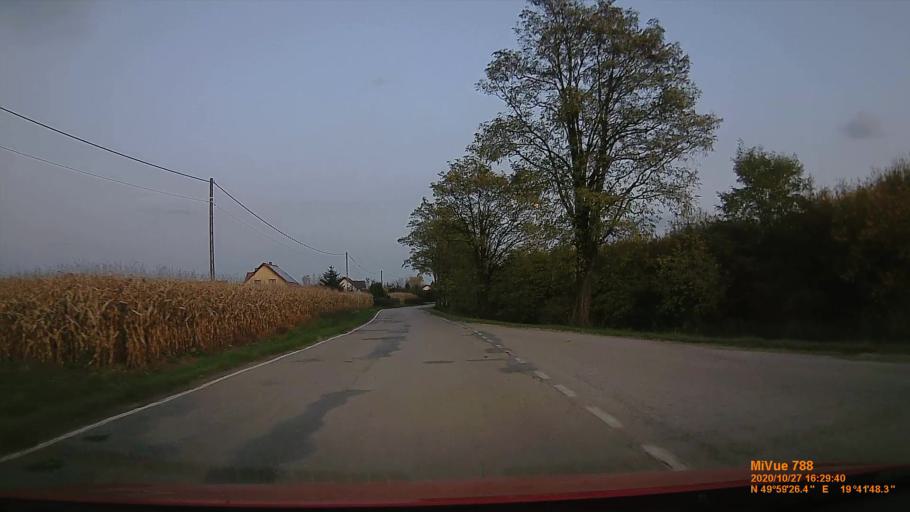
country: PL
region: Lesser Poland Voivodeship
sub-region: Powiat krakowski
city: Czernichow
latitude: 49.9906
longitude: 19.6969
